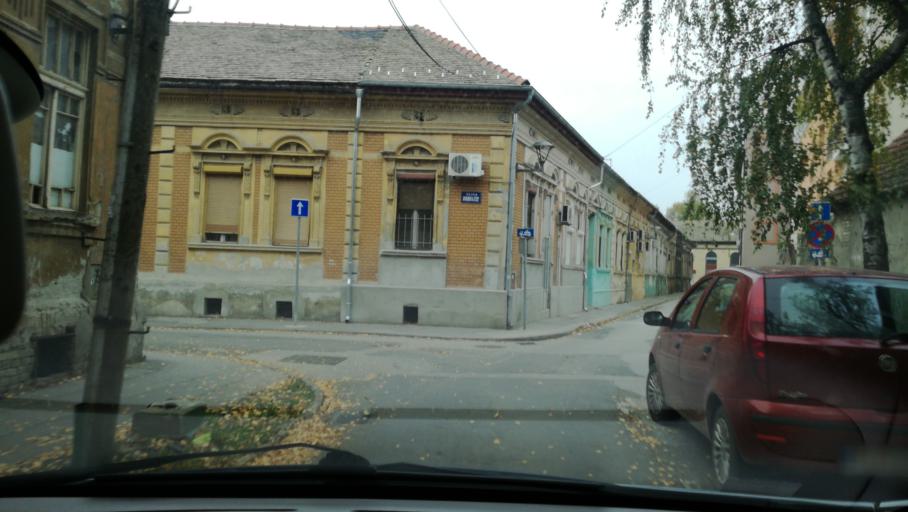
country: RS
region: Autonomna Pokrajina Vojvodina
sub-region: Juznobacki Okrug
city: Novi Sad
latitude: 45.2600
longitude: 19.8416
